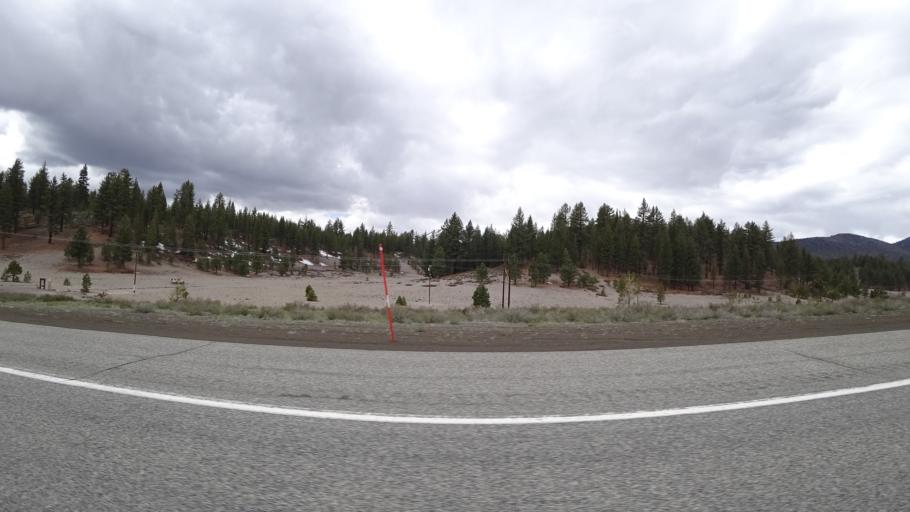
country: US
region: California
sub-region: Mono County
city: Mammoth Lakes
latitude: 37.7647
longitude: -119.0000
